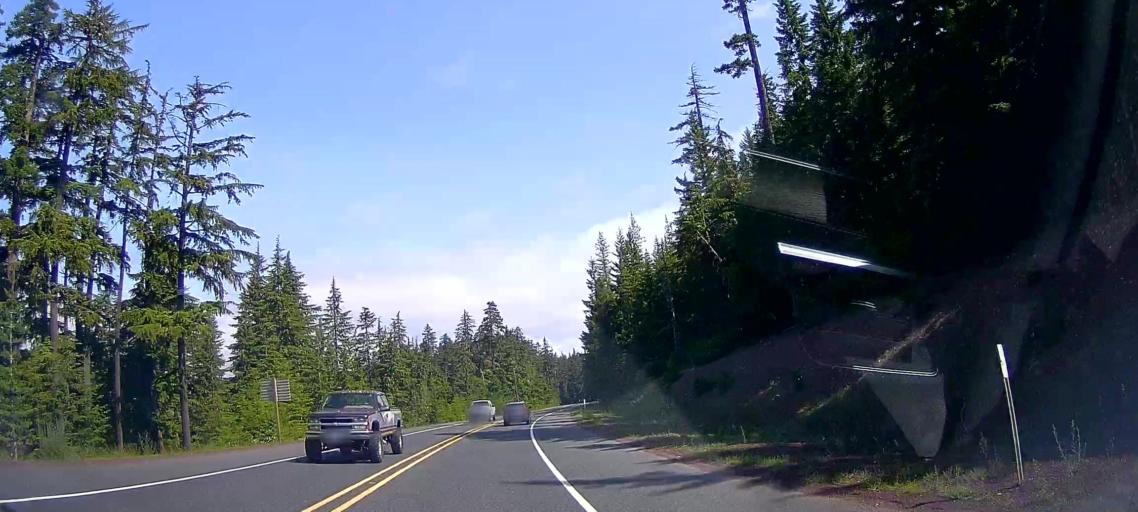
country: US
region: Oregon
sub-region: Clackamas County
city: Mount Hood Village
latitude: 45.1974
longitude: -121.6922
